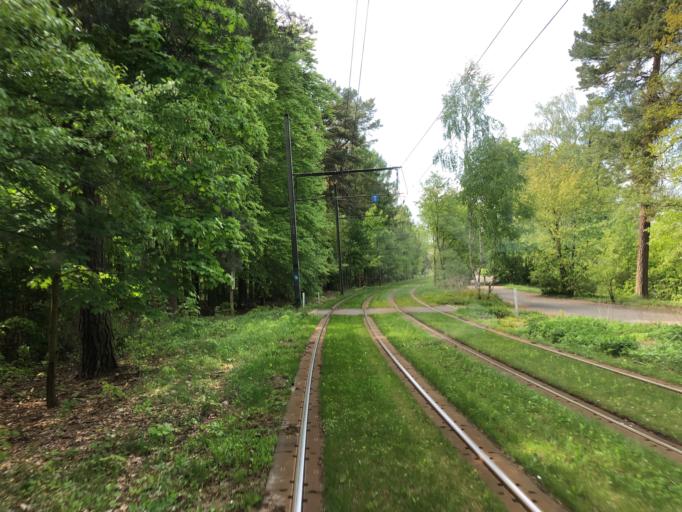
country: DE
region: Berlin
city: Grunau
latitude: 52.4071
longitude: 13.6112
